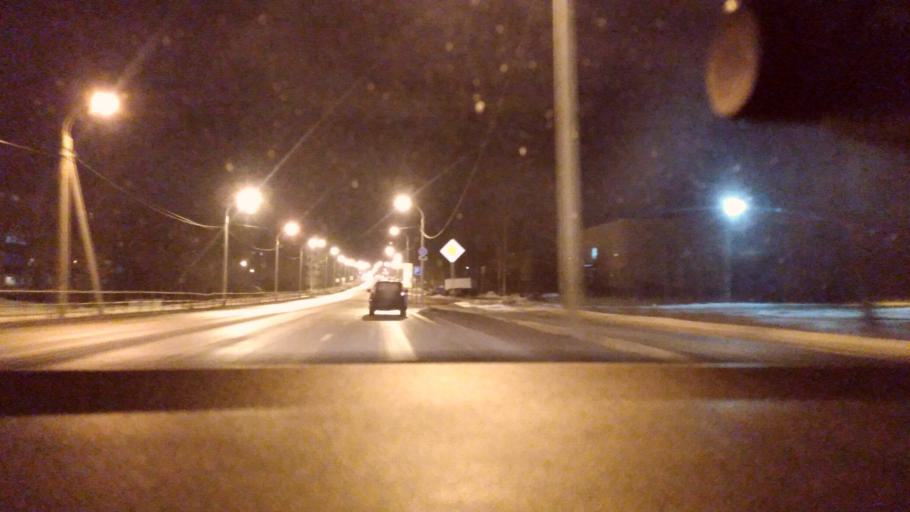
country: RU
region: Moskovskaya
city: Yegor'yevsk
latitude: 55.3712
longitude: 39.0684
